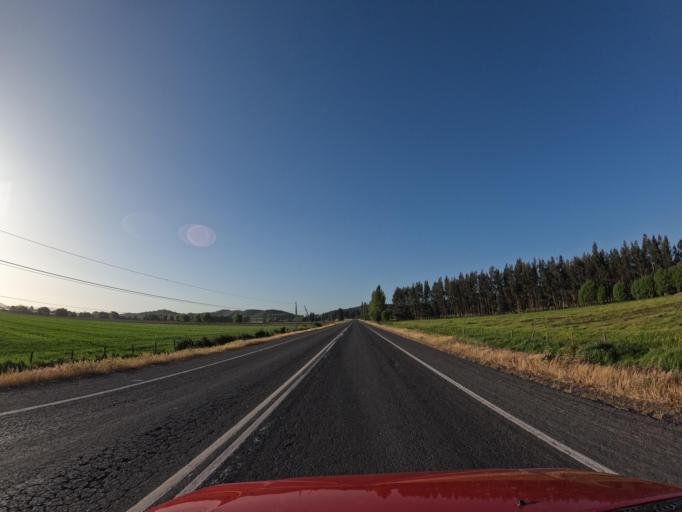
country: CL
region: O'Higgins
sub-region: Provincia de Colchagua
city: Santa Cruz
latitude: -34.4383
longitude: -71.3682
